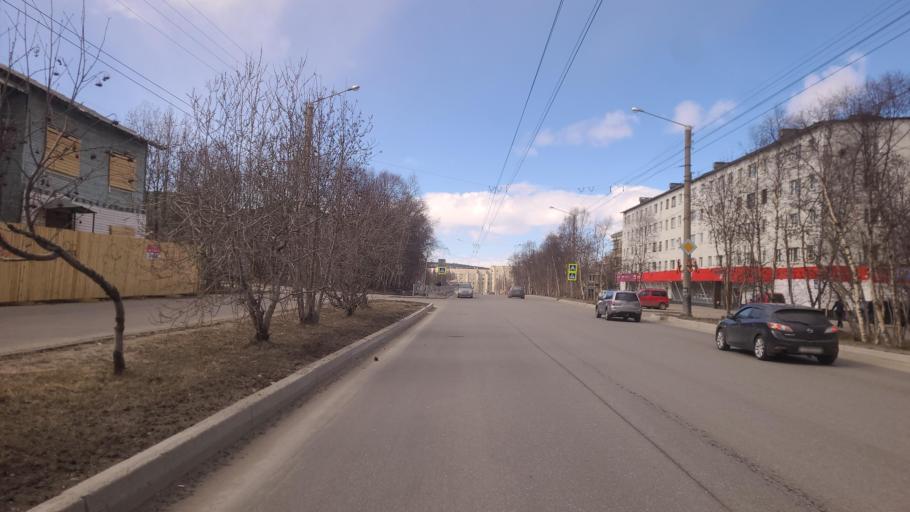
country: RU
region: Murmansk
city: Murmansk
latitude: 68.9527
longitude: 33.0707
